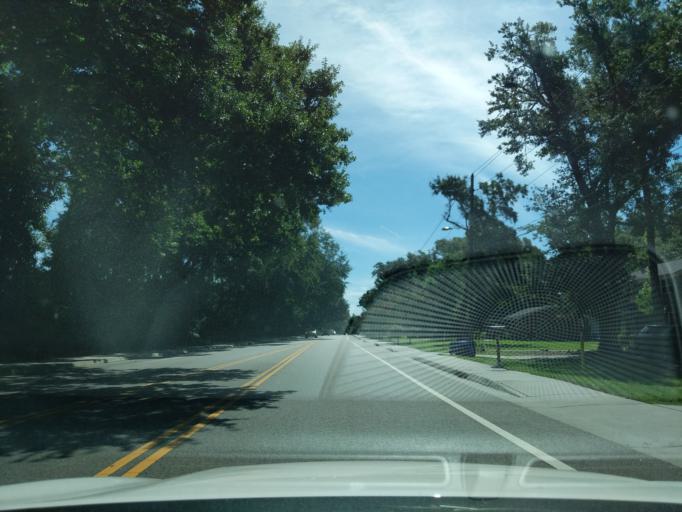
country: US
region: South Carolina
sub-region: Charleston County
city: Charleston
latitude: 32.7423
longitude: -79.9338
